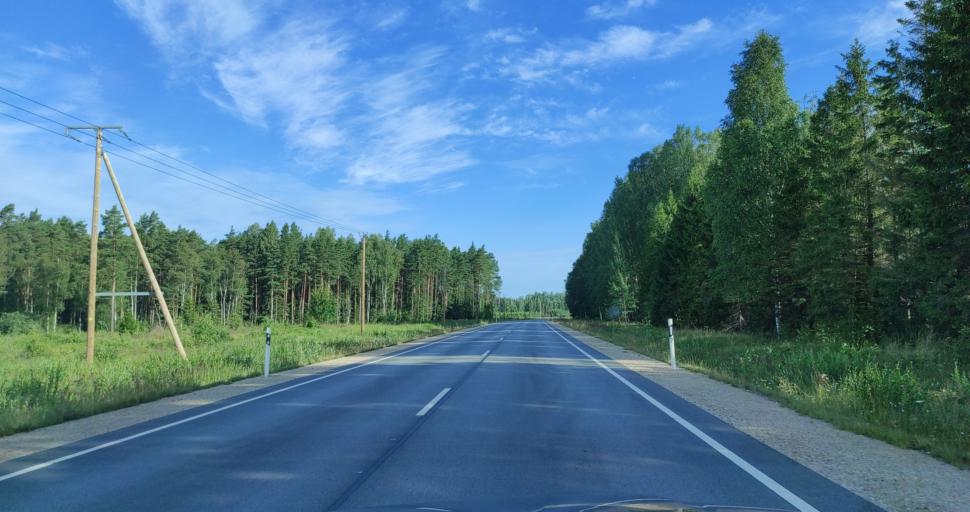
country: LV
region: Pavilostas
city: Pavilosta
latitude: 56.8021
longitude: 21.2289
